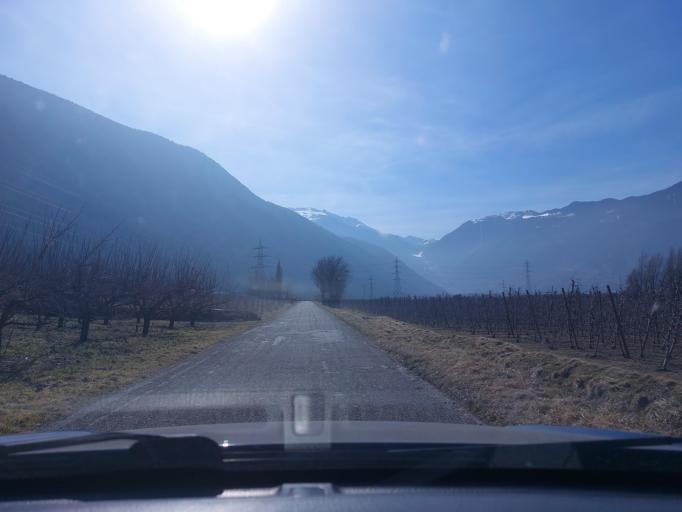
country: CH
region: Valais
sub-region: Martigny District
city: Charrat-les-Chenes
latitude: 46.1161
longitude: 7.1224
